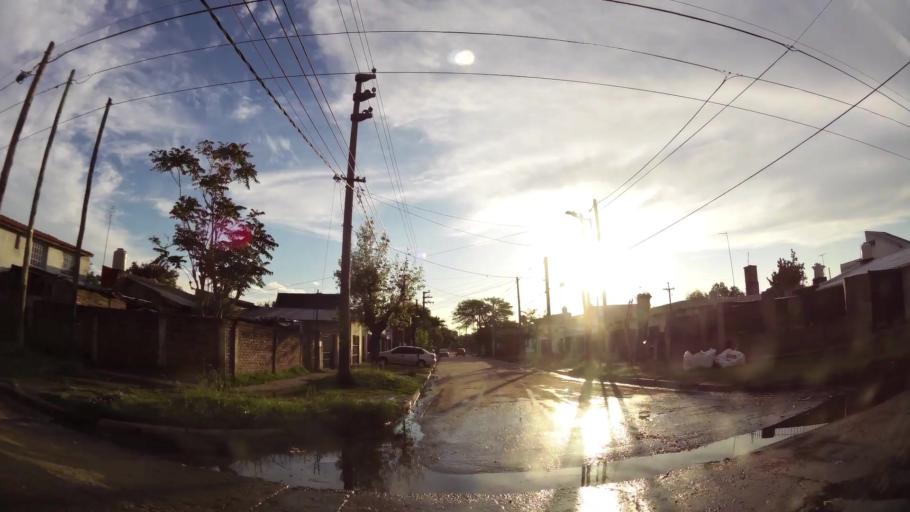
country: AR
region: Buenos Aires
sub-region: Partido de Almirante Brown
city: Adrogue
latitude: -34.7617
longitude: -58.3540
